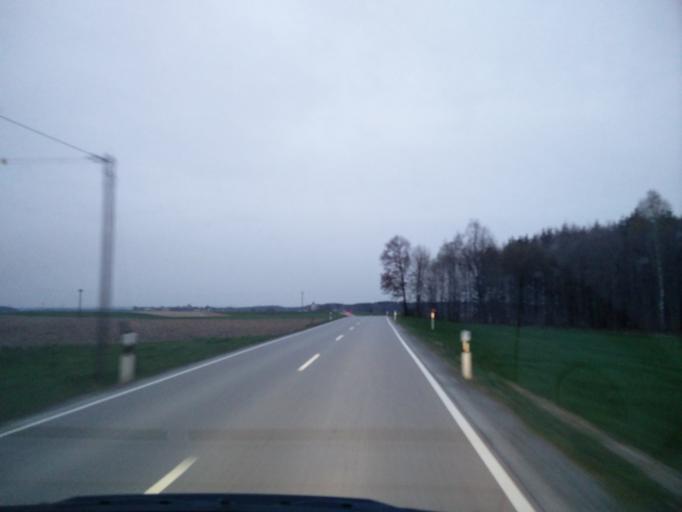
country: DE
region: Bavaria
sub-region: Upper Bavaria
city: Albaching
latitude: 48.1148
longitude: 12.0974
